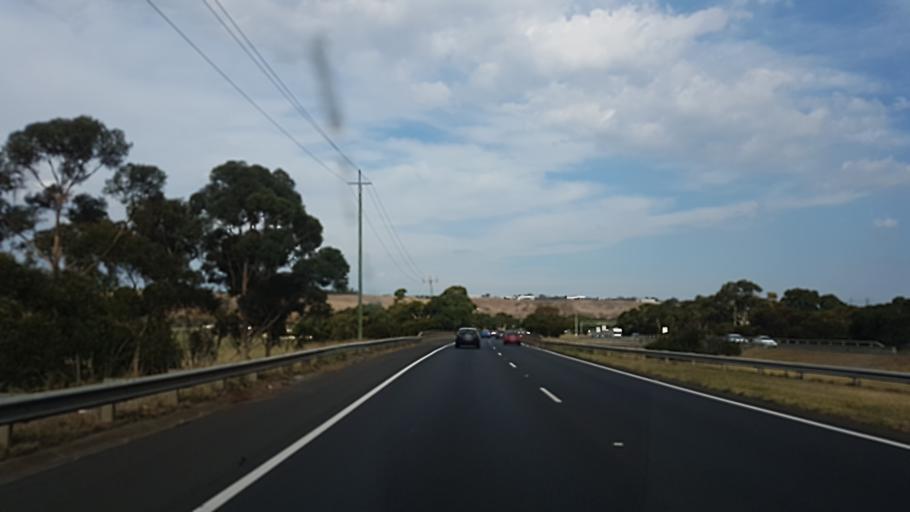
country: AU
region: Victoria
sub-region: Brimbank
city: Keilor
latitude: -37.7116
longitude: 144.8302
